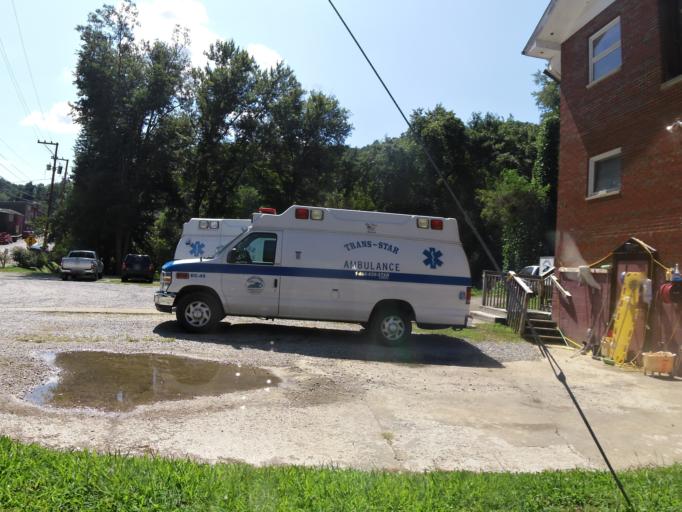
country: US
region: Kentucky
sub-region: Leslie County
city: Hyden
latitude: 37.1638
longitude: -83.3746
